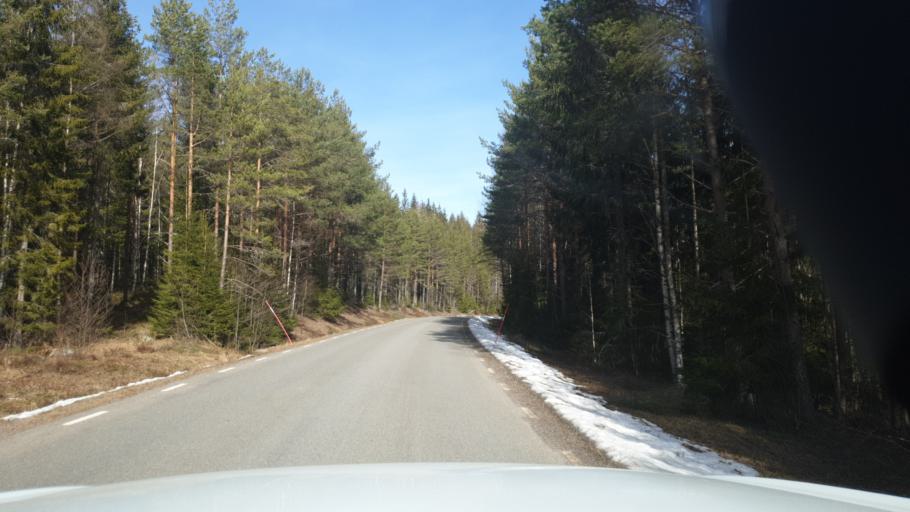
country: SE
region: Vaermland
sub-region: Arvika Kommun
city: Arvika
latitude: 59.5477
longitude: 12.4021
